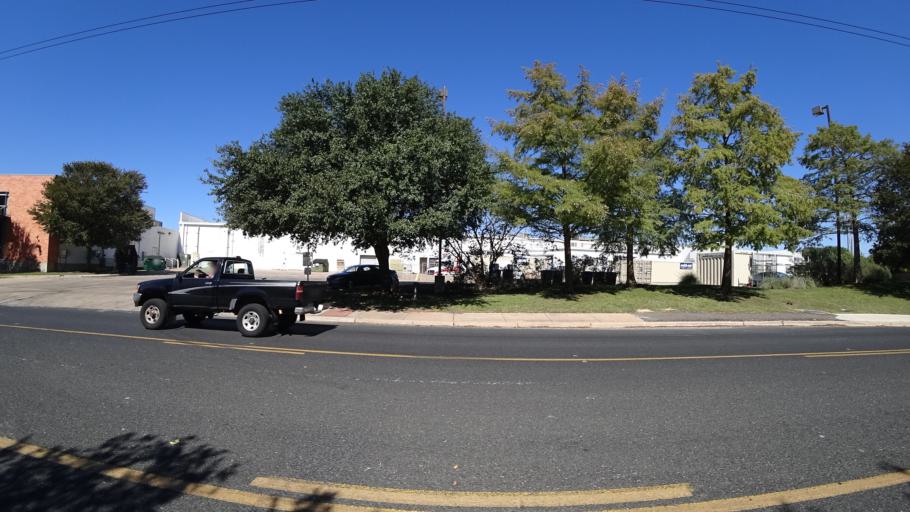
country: US
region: Texas
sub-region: Travis County
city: Rollingwood
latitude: 30.2301
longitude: -97.7979
